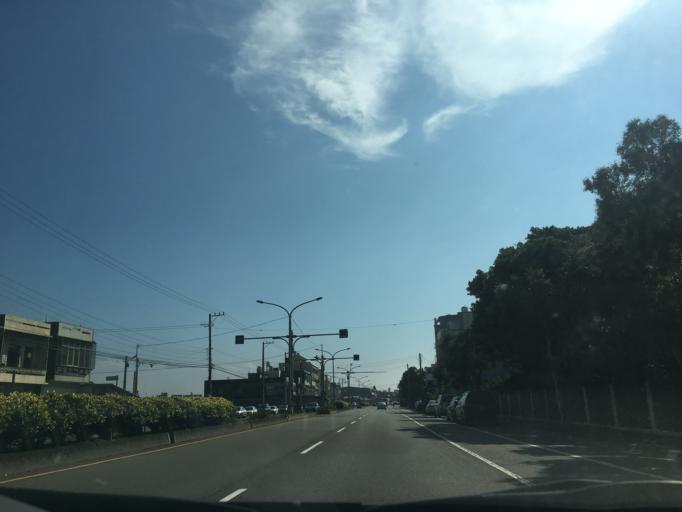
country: TW
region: Taiwan
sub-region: Hsinchu
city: Hsinchu
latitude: 24.8241
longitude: 120.9271
